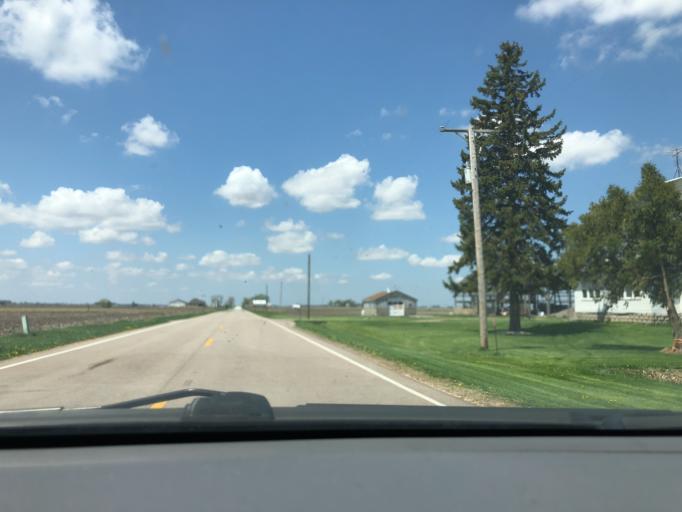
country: US
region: Illinois
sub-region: Kane County
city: Hampshire
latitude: 42.1100
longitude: -88.5835
